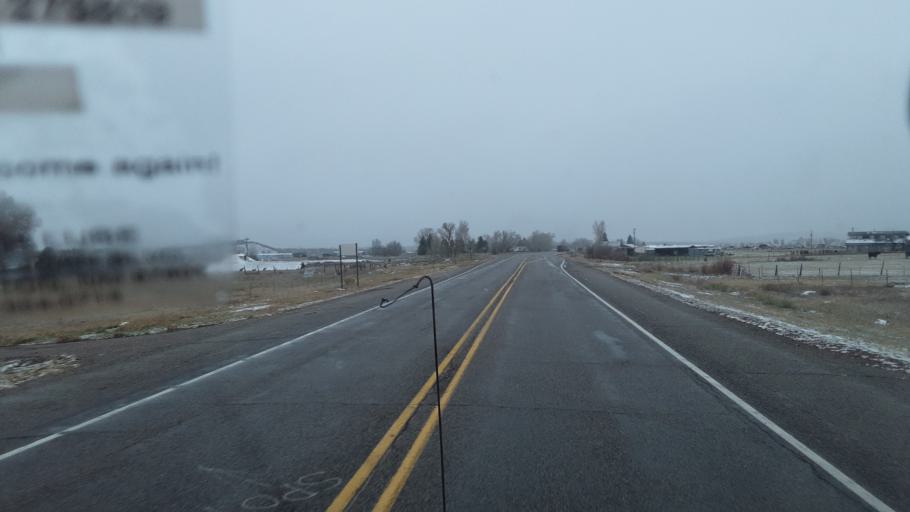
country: US
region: New Mexico
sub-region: Rio Arriba County
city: Tierra Amarilla
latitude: 36.7345
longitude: -106.5677
